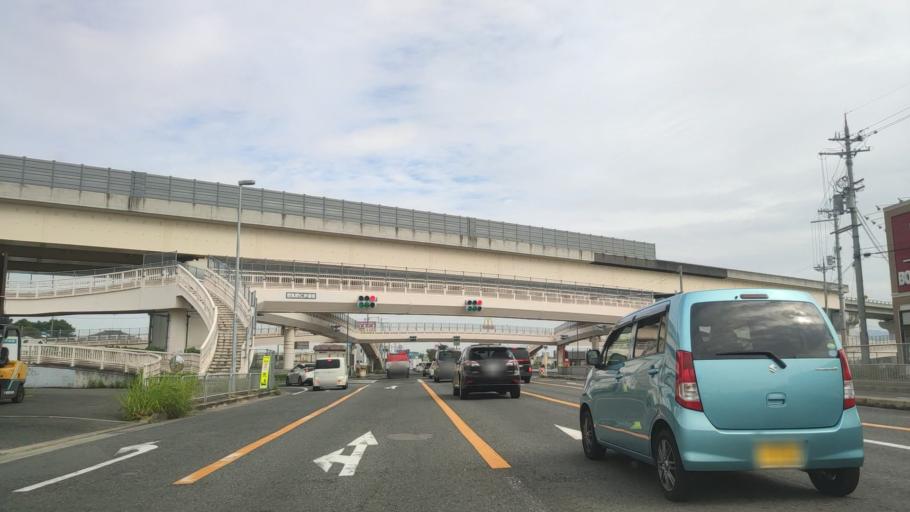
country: JP
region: Osaka
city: Tondabayashicho
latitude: 34.5331
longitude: 135.6048
